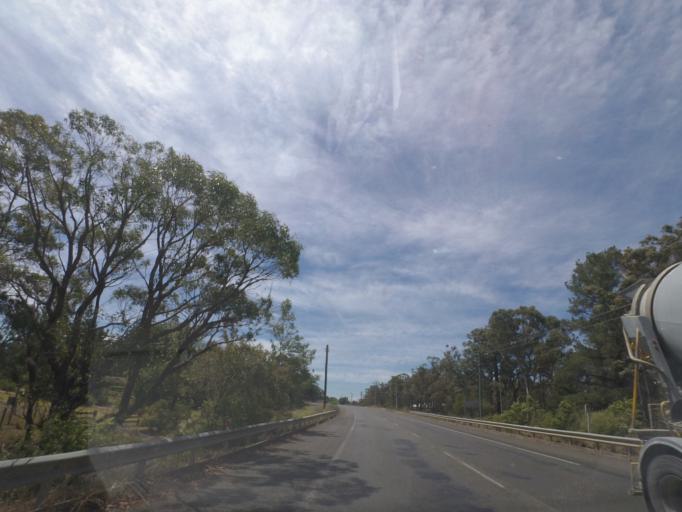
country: AU
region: New South Wales
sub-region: Wollondilly
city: Buxton
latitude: -34.2604
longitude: 150.5739
